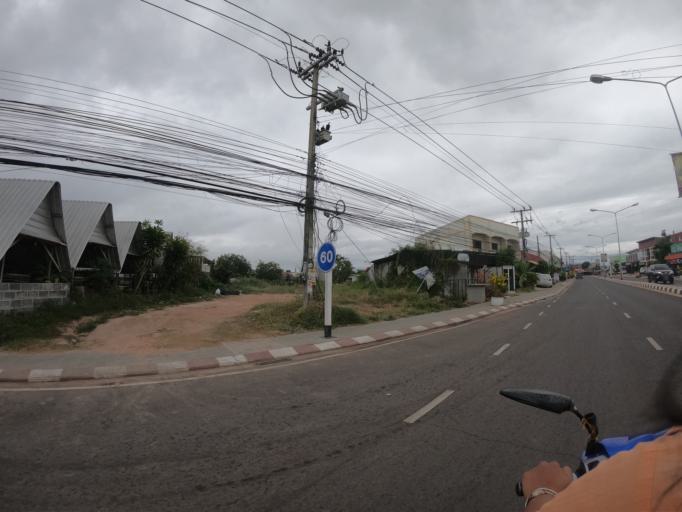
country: TH
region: Roi Et
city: Chiang Khwan
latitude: 16.1522
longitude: 103.8645
